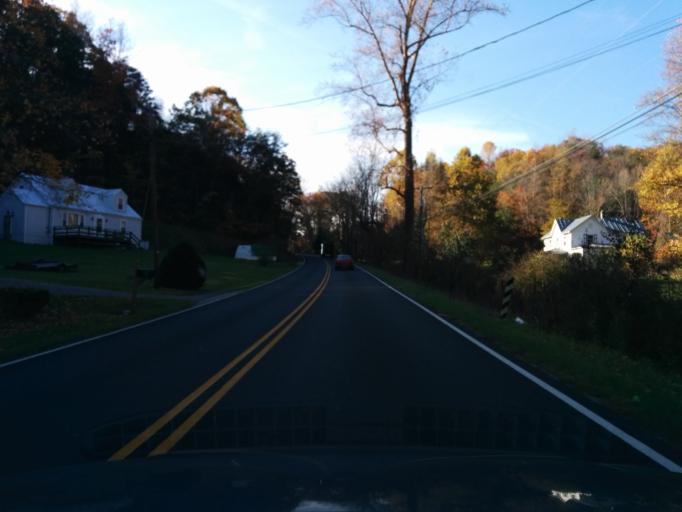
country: US
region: Virginia
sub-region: City of Lexington
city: Lexington
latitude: 37.8345
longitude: -79.4941
